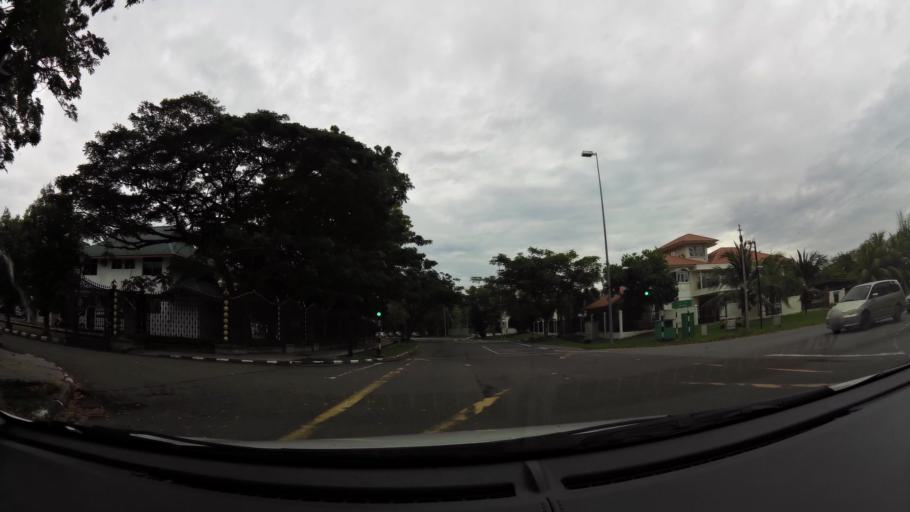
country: BN
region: Brunei and Muara
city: Bandar Seri Begawan
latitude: 4.8976
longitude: 114.9239
